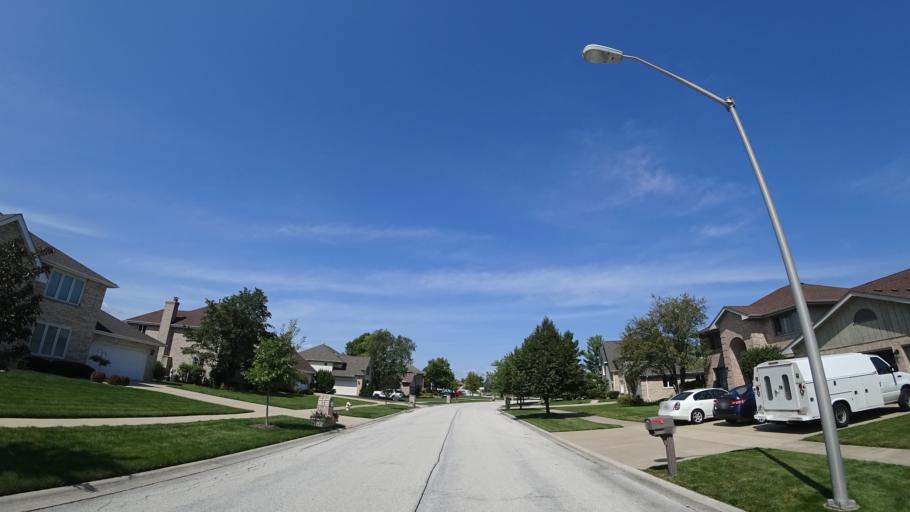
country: US
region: Illinois
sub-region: Cook County
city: Orland Hills
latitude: 41.5628
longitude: -87.8361
